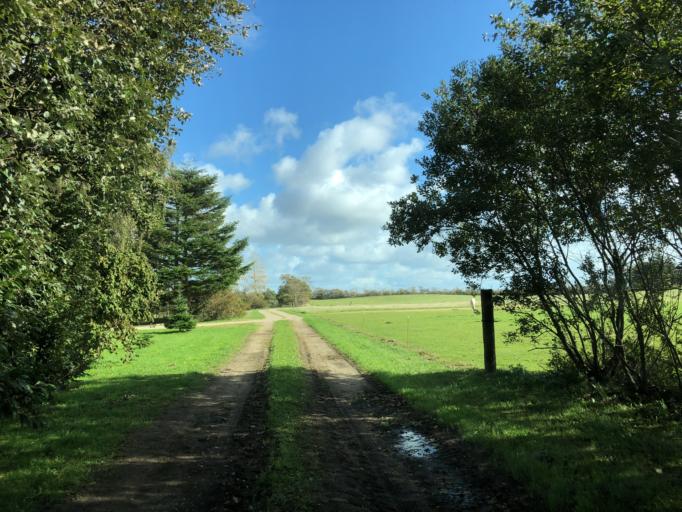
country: DK
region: Central Jutland
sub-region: Holstebro Kommune
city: Ulfborg
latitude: 56.2938
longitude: 8.3201
